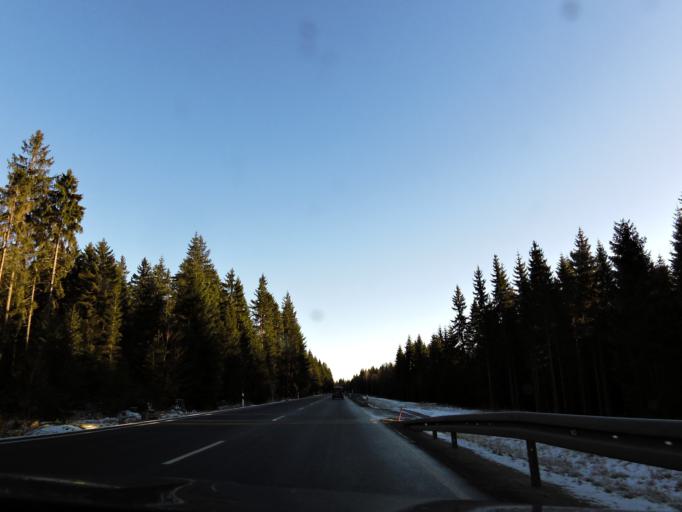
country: DE
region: Bavaria
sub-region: Upper Franconia
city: Fichtelberg
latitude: 50.0249
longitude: 11.8616
